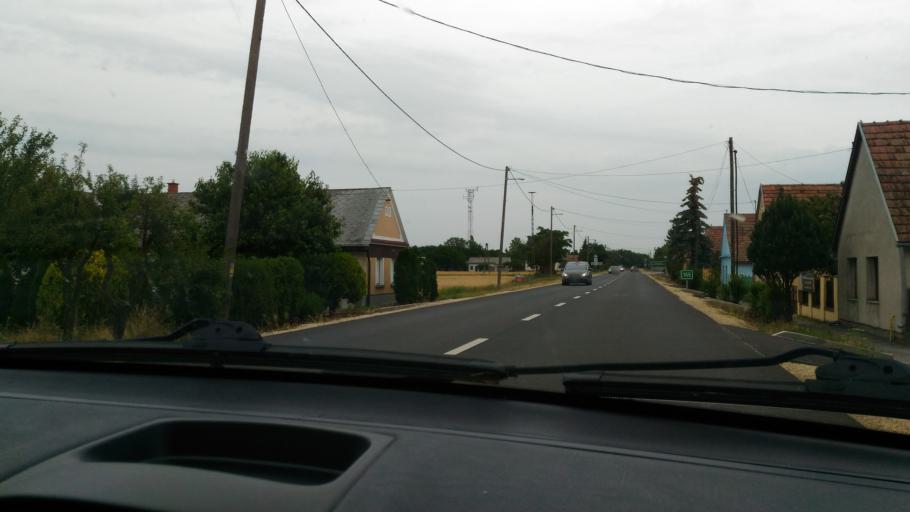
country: HU
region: Vas
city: Kormend
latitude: 47.0513
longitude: 16.6900
